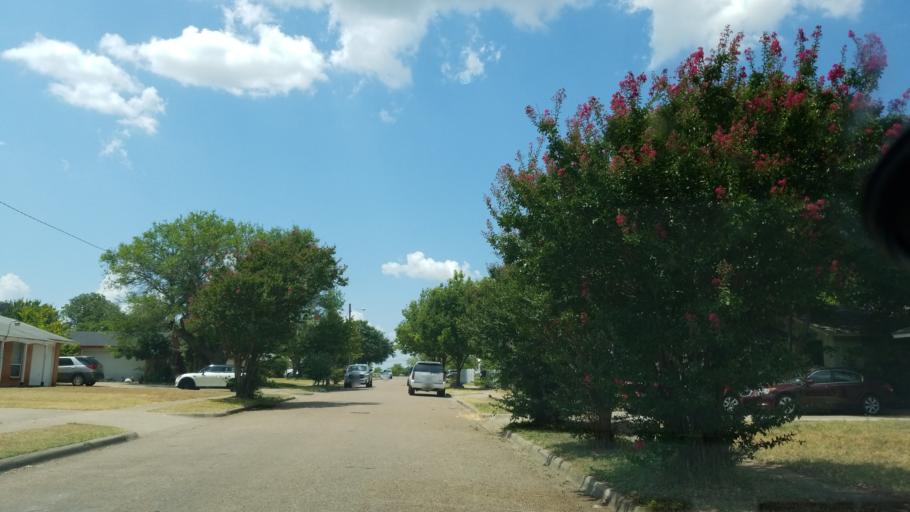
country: US
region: Texas
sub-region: Dallas County
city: Cockrell Hill
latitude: 32.7190
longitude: -96.8974
